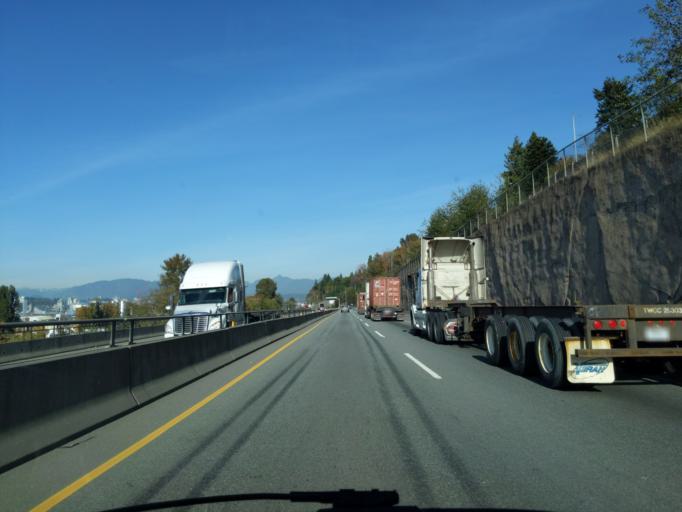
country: CA
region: British Columbia
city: Delta
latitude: 49.1708
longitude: -122.9198
